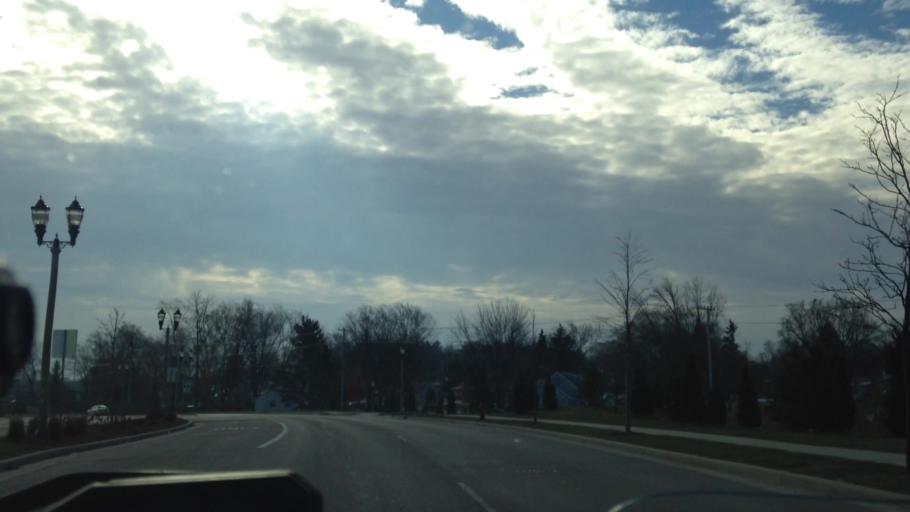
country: US
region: Wisconsin
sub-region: Waukesha County
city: Menomonee Falls
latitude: 43.1828
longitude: -88.1065
